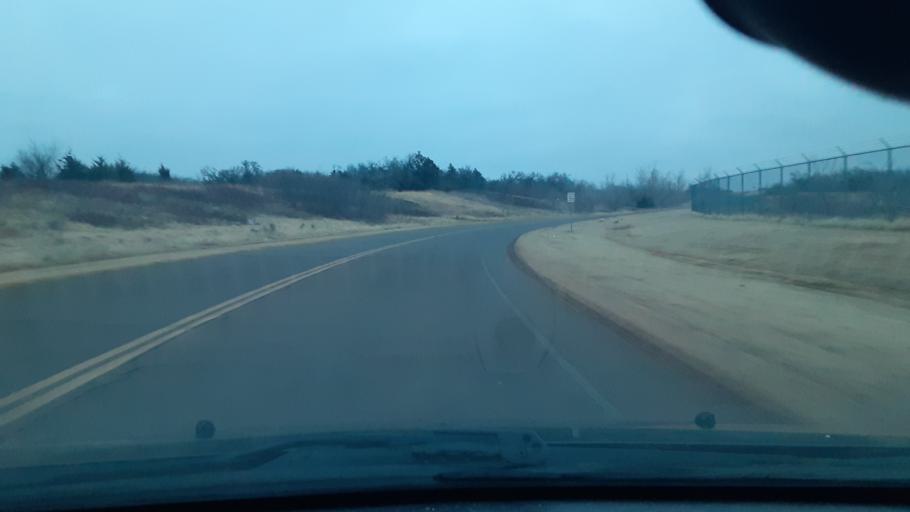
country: US
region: Oklahoma
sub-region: Logan County
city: Guthrie
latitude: 35.8613
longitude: -97.4164
